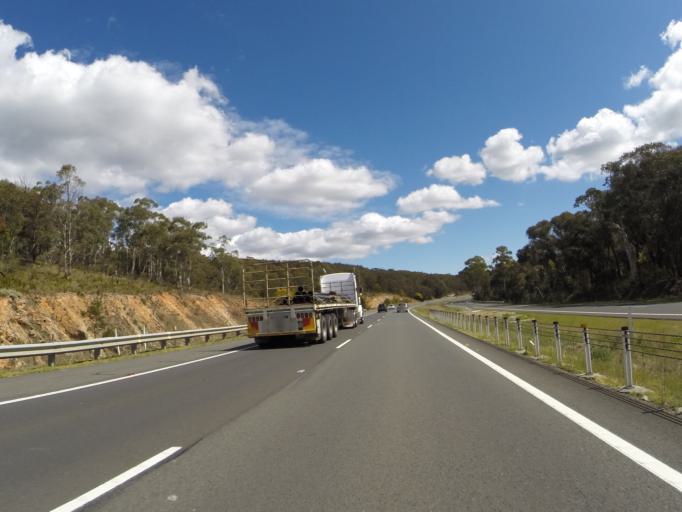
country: AU
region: New South Wales
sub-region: Goulburn Mulwaree
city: Goulburn
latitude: -34.7443
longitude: 149.9282
